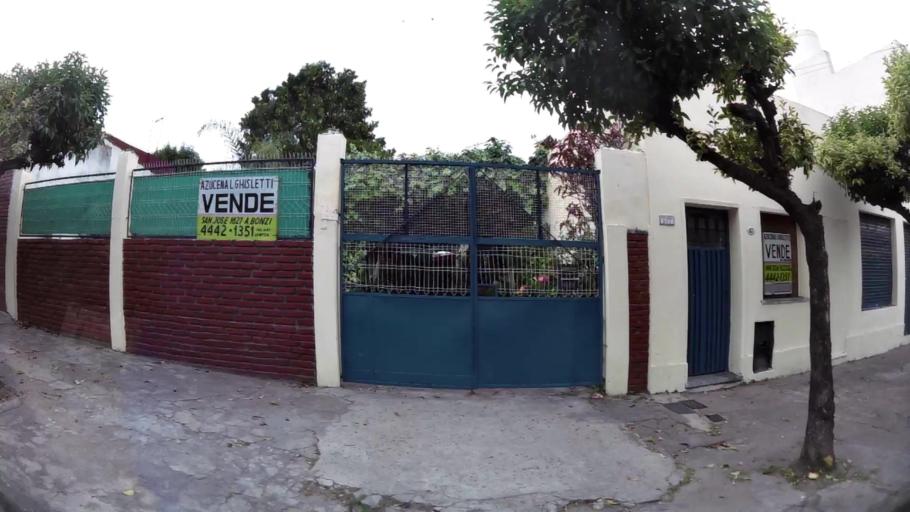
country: AR
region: Buenos Aires F.D.
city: Villa Lugano
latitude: -34.6743
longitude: -58.5153
